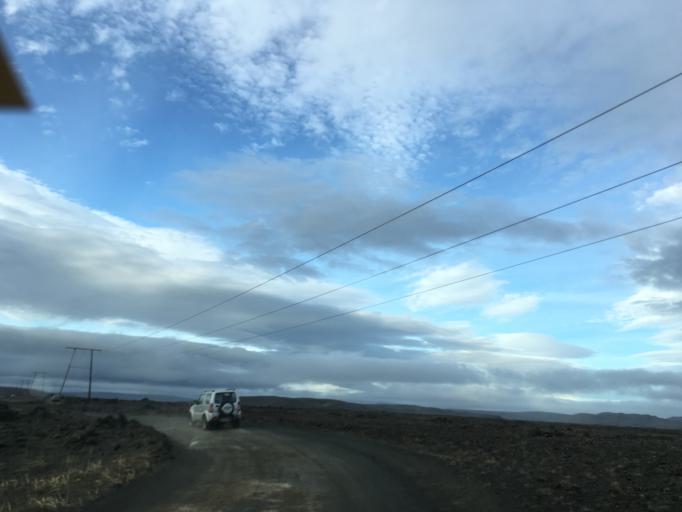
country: IS
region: South
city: Vestmannaeyjar
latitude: 64.1366
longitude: -19.1269
